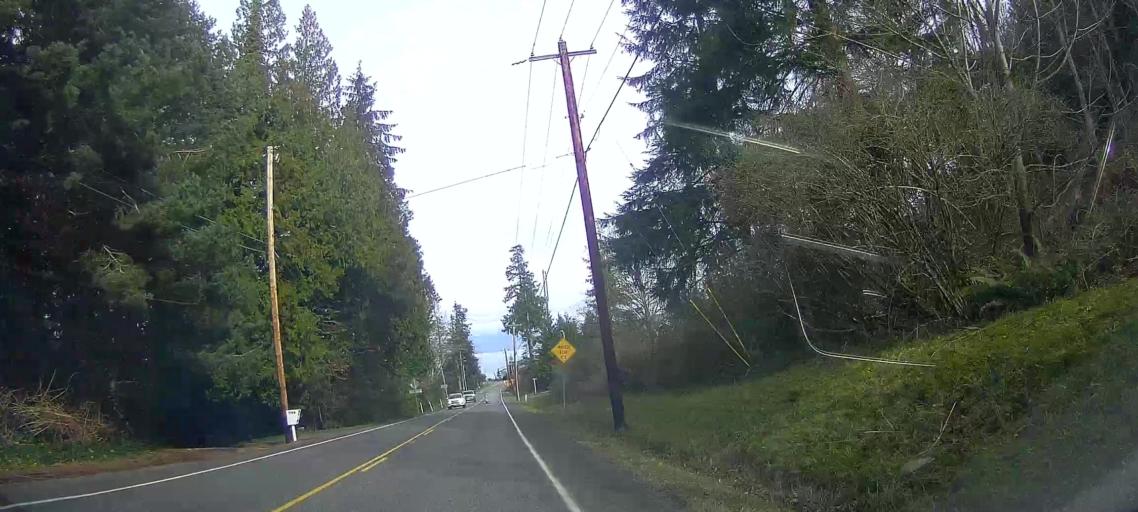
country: US
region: Washington
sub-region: Island County
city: Camano
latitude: 48.2530
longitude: -122.5083
